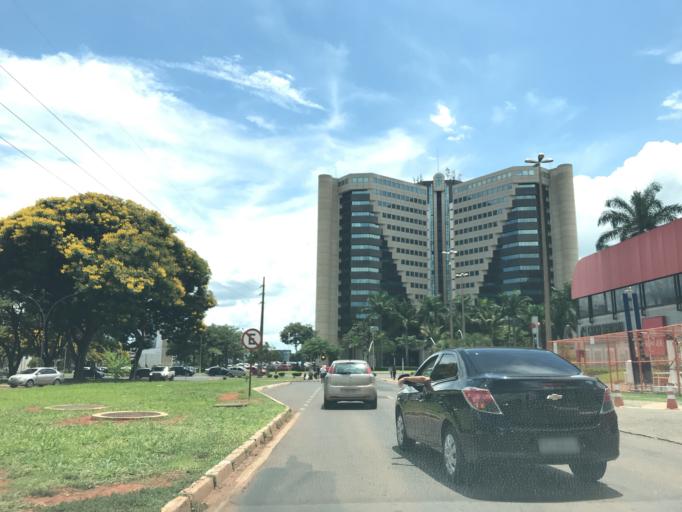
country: BR
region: Federal District
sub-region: Brasilia
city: Brasilia
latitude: -15.7860
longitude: -47.8890
